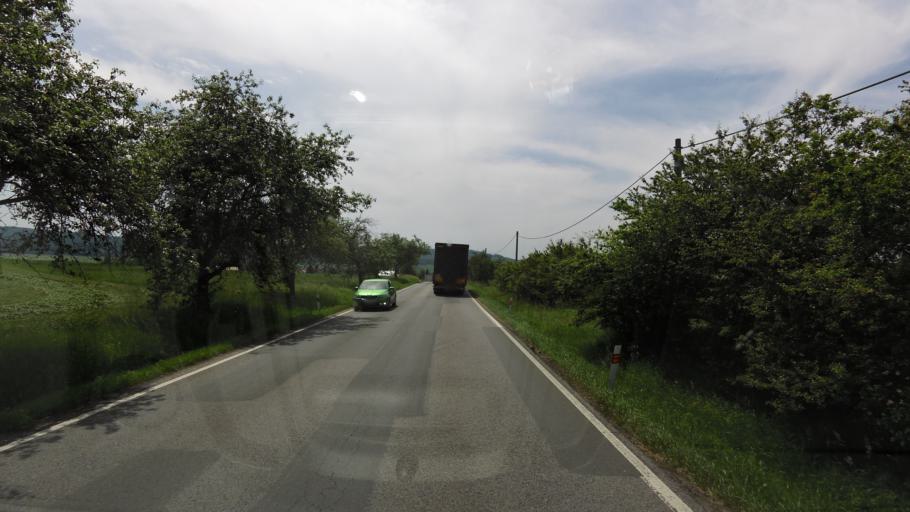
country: CZ
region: Plzensky
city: Myto
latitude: 49.7961
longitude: 13.7444
